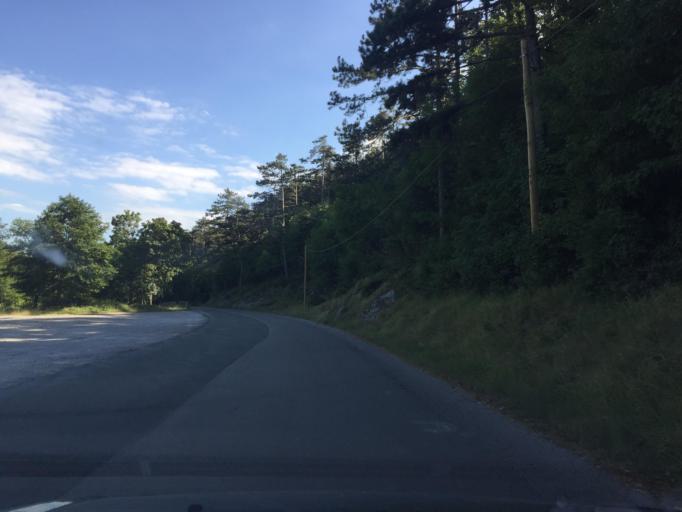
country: HR
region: Primorsko-Goranska
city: Klana
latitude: 45.4574
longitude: 14.3779
